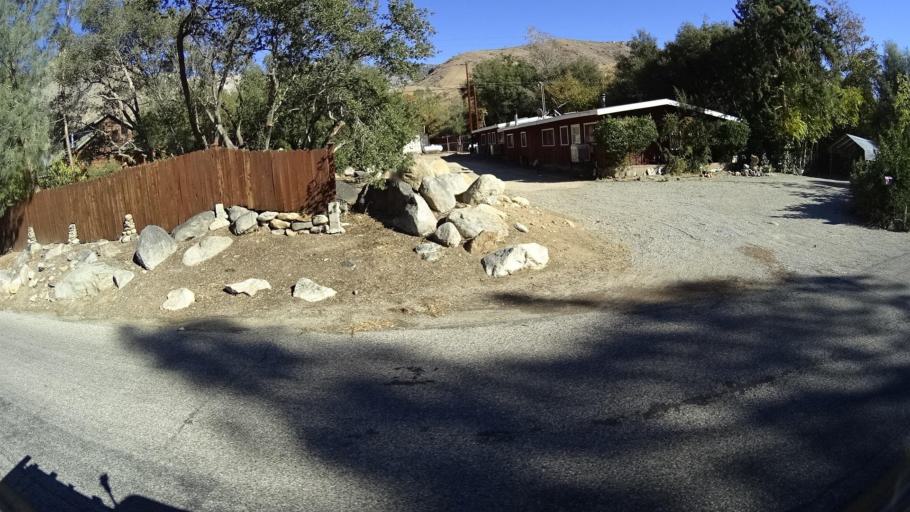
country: US
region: California
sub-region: Kern County
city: Kernville
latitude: 35.7894
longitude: -118.4479
